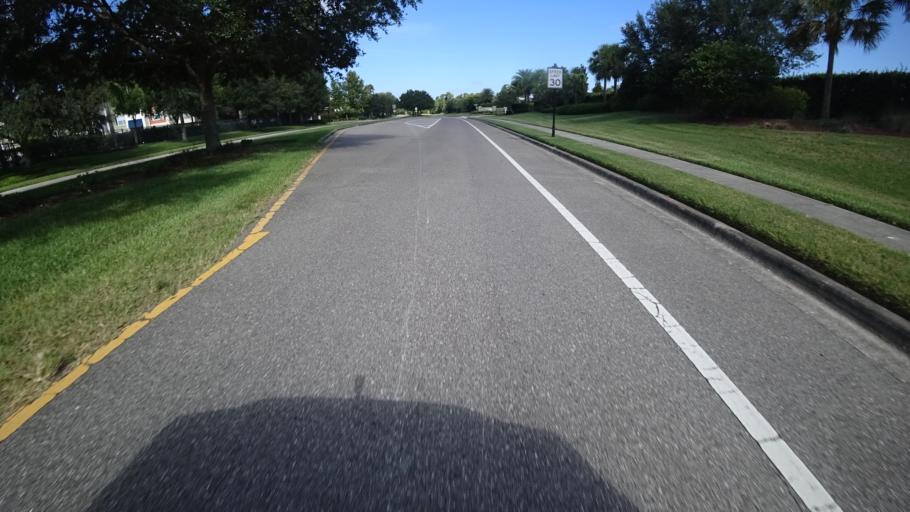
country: US
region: Florida
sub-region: Manatee County
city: Ellenton
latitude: 27.5058
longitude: -82.4763
